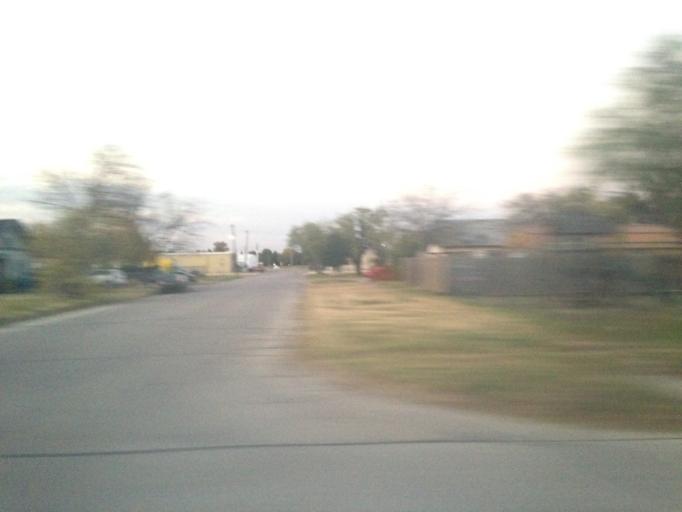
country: US
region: Texas
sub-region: Taylor County
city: Abilene
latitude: 32.4470
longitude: -99.7404
